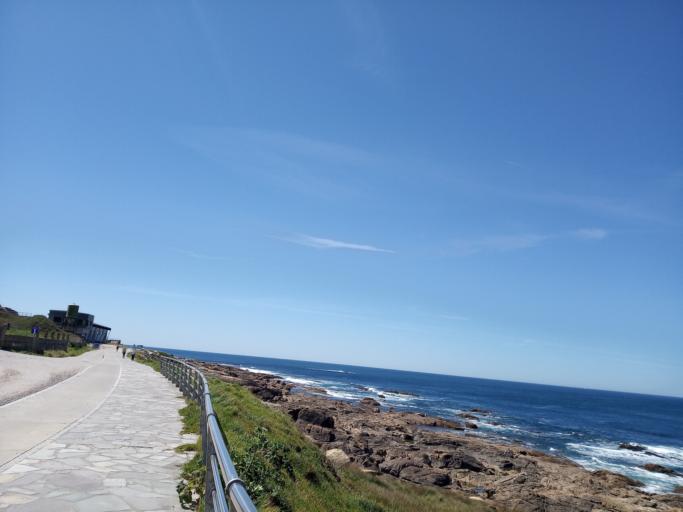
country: ES
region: Galicia
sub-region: Provincia de Pontevedra
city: A Guarda
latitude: 41.8894
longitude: -8.8803
